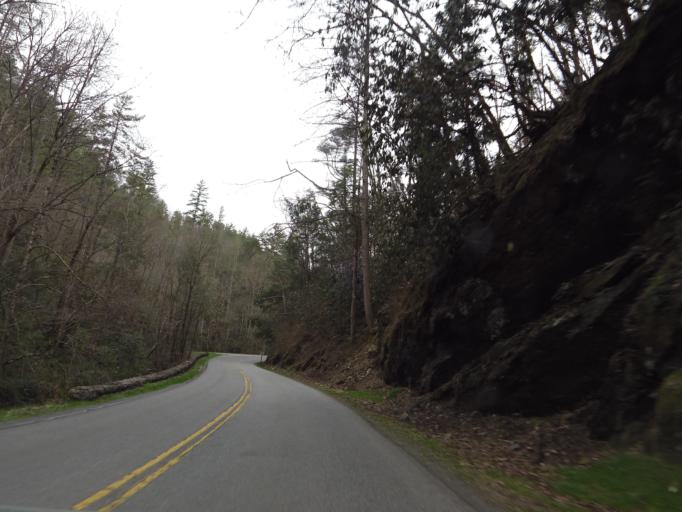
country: US
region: Tennessee
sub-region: Blount County
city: Wildwood
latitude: 35.6384
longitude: -83.7230
